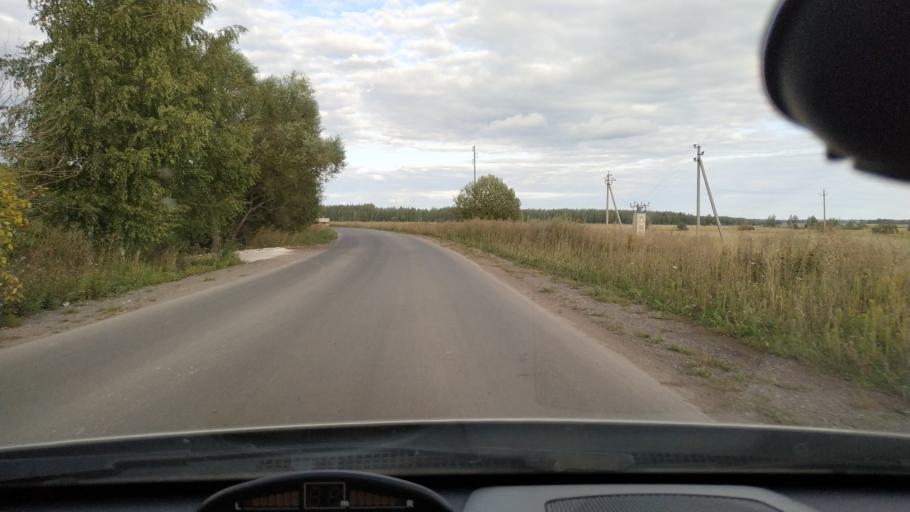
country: RU
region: Rjazan
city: Polyany
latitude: 54.5765
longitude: 39.8525
